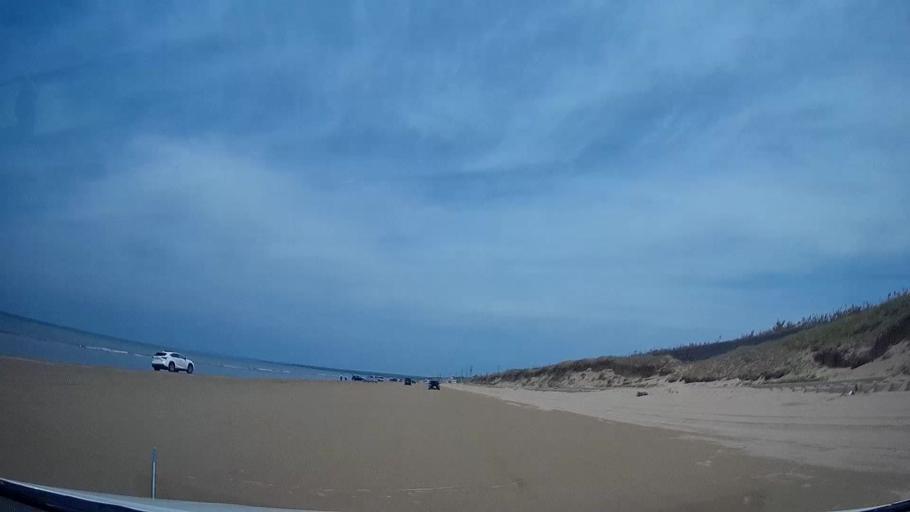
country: JP
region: Ishikawa
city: Hakui
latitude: 36.8480
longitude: 136.7525
